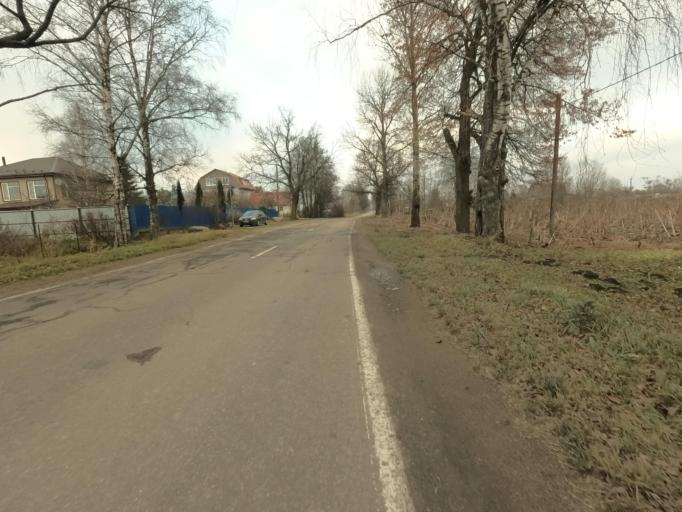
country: RU
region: Leningrad
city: Mga
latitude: 59.7837
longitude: 31.0241
